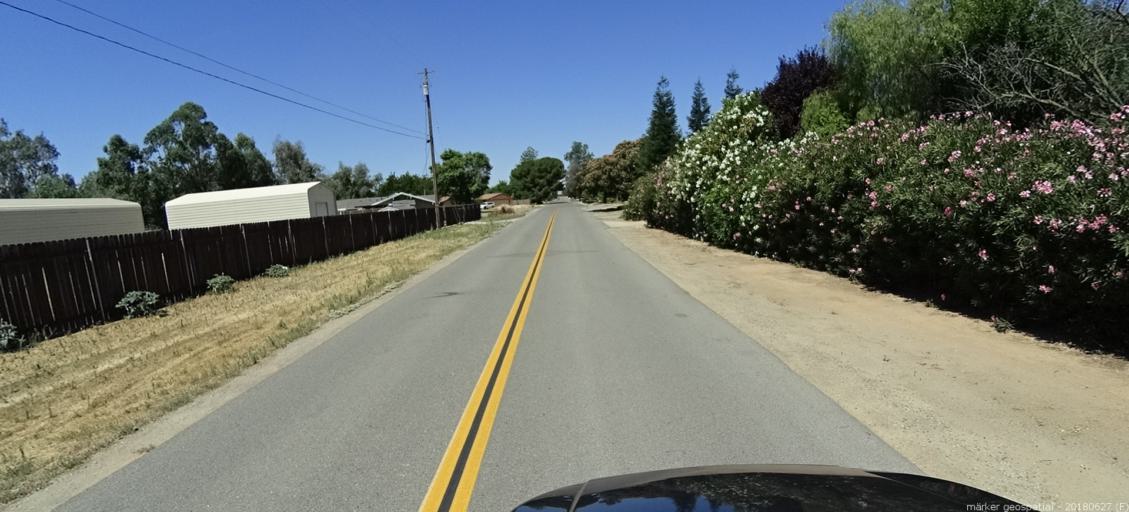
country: US
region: California
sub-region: Madera County
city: Bonadelle Ranchos-Madera Ranchos
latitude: 36.9201
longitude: -119.8870
